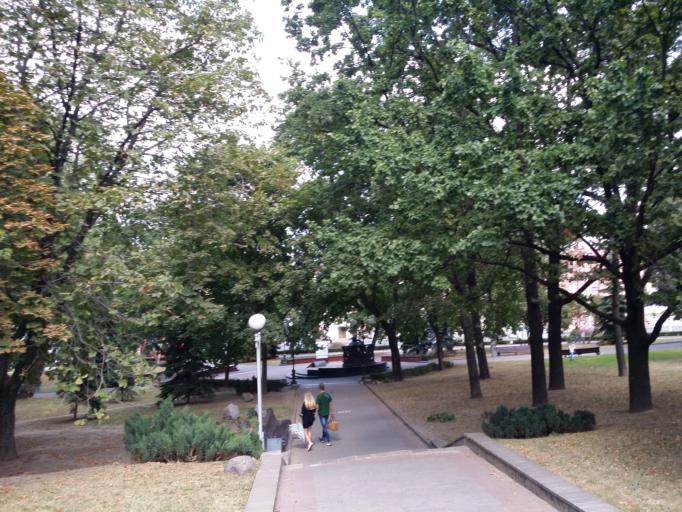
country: BY
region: Minsk
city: Minsk
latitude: 53.9002
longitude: 27.5495
